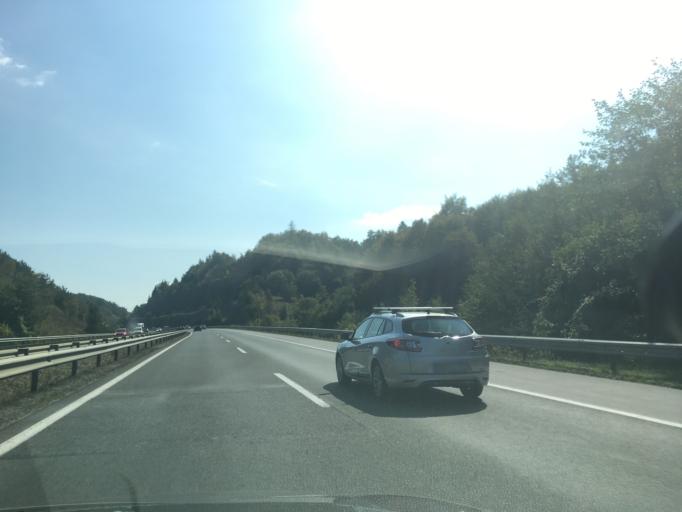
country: SI
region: Skofljica
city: Skofljica
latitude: 45.9999
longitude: 14.5837
